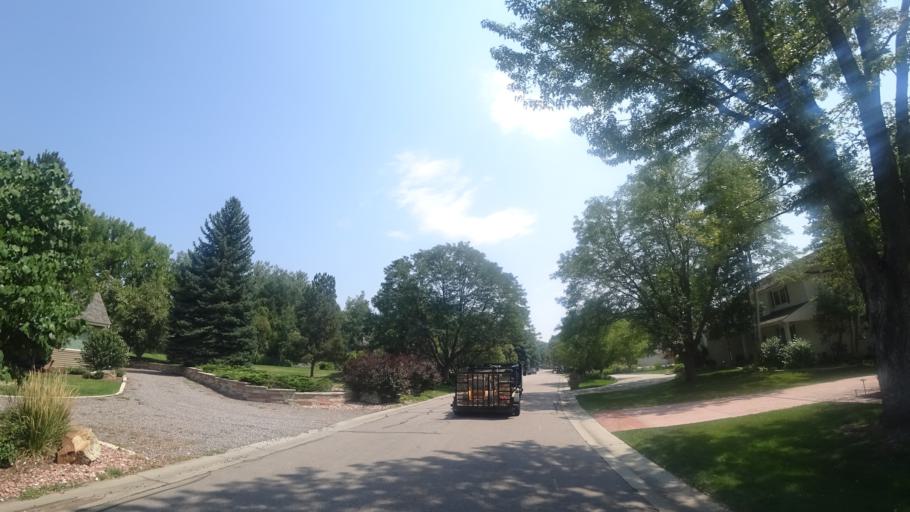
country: US
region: Colorado
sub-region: Arapahoe County
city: Greenwood Village
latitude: 39.6141
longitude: -104.9733
